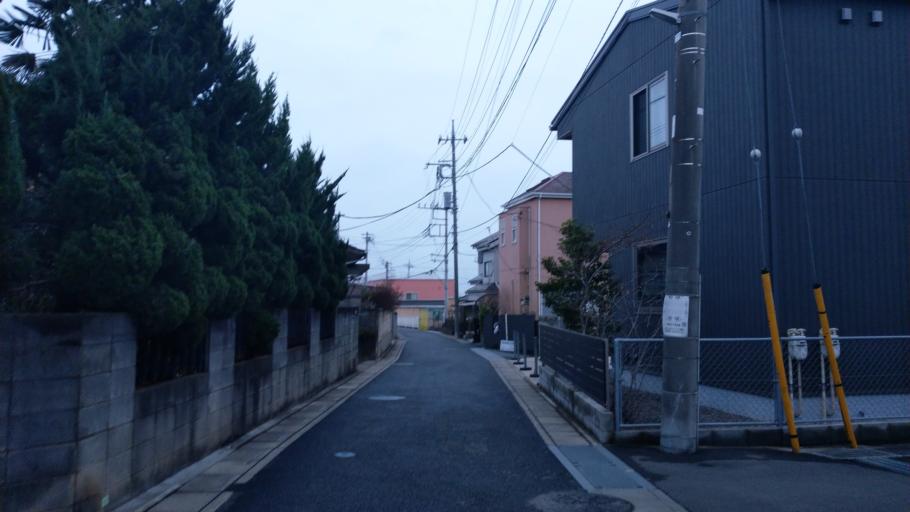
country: JP
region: Saitama
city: Yono
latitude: 35.9009
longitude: 139.5892
